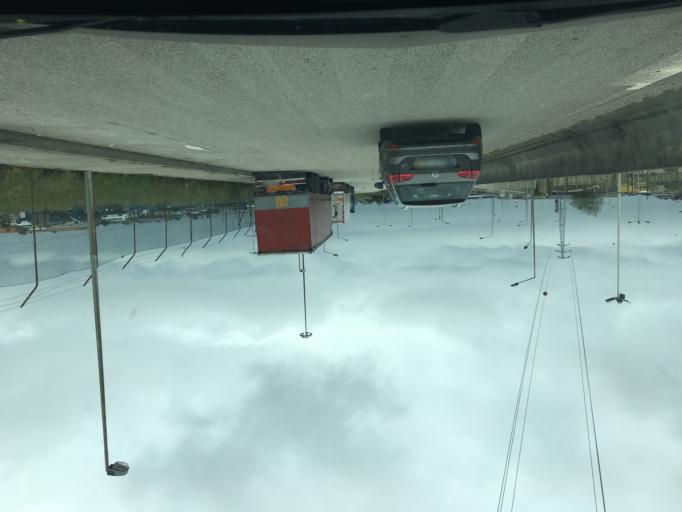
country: PT
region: Porto
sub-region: Matosinhos
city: Santa Cruz do Bispo
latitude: 41.2170
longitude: -8.6875
